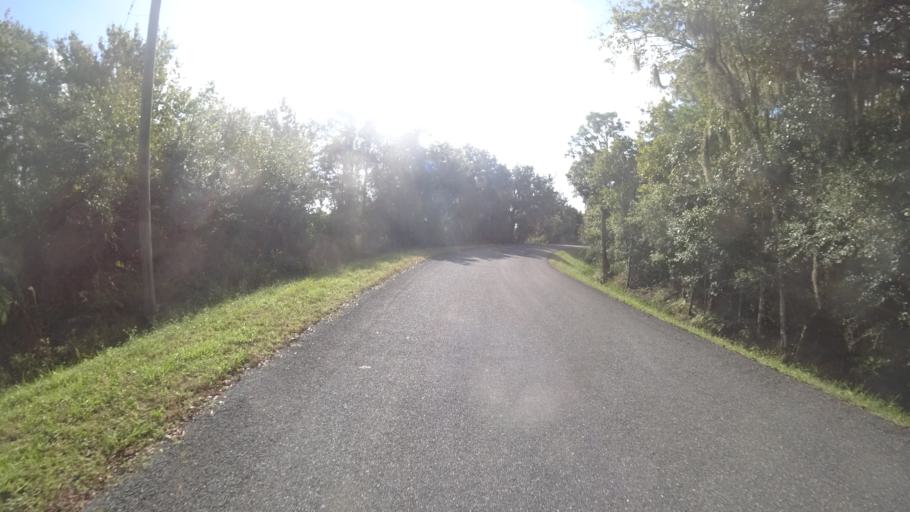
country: US
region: Florida
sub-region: Hillsborough County
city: Wimauma
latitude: 27.4740
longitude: -82.1535
